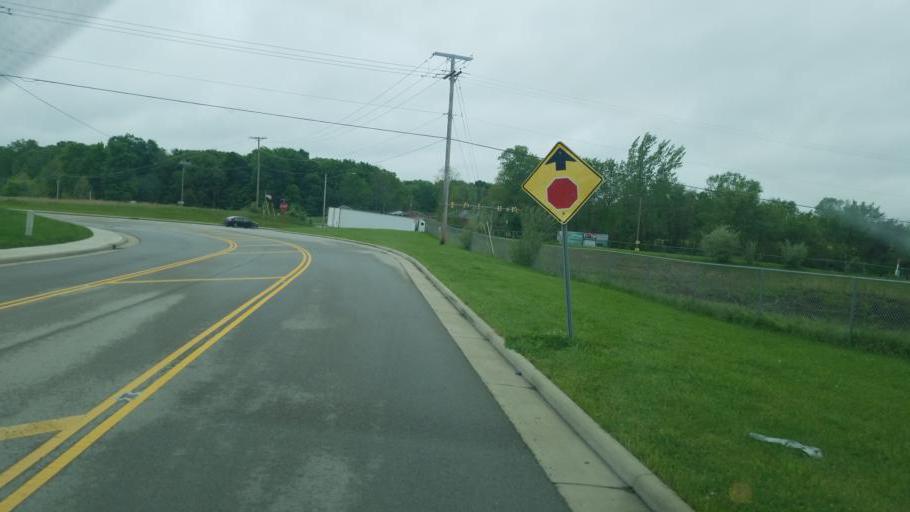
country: US
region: Ohio
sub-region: Highland County
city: Hillsboro
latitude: 39.2258
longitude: -83.6248
